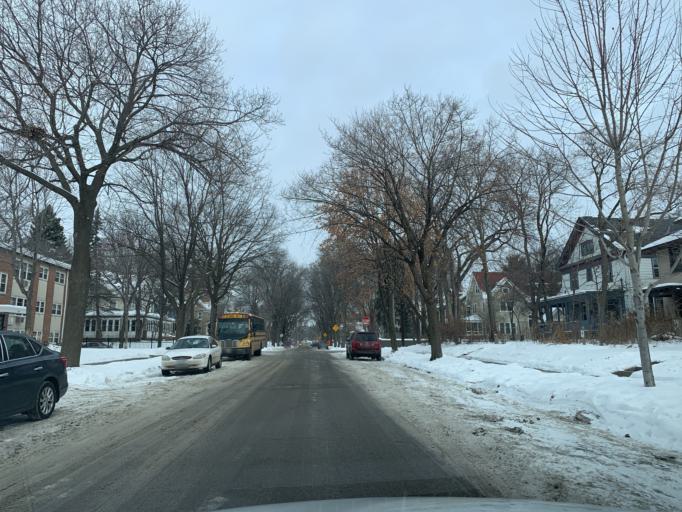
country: US
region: Minnesota
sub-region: Hennepin County
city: Minneapolis
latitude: 44.9568
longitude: -93.2829
